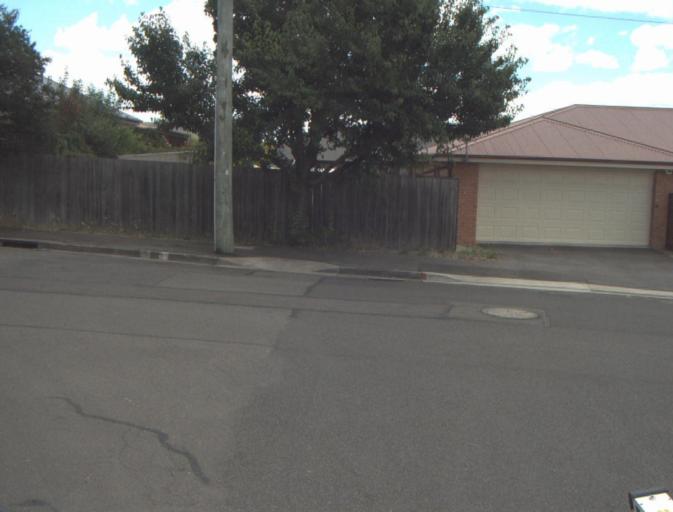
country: AU
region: Tasmania
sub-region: Launceston
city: Newstead
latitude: -41.4373
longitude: 147.1606
